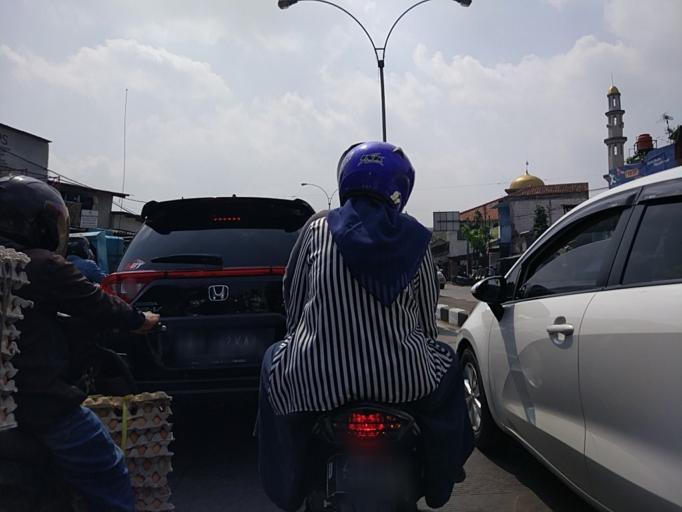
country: ID
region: West Java
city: Margahayukencana
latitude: -6.9236
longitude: 107.5749
